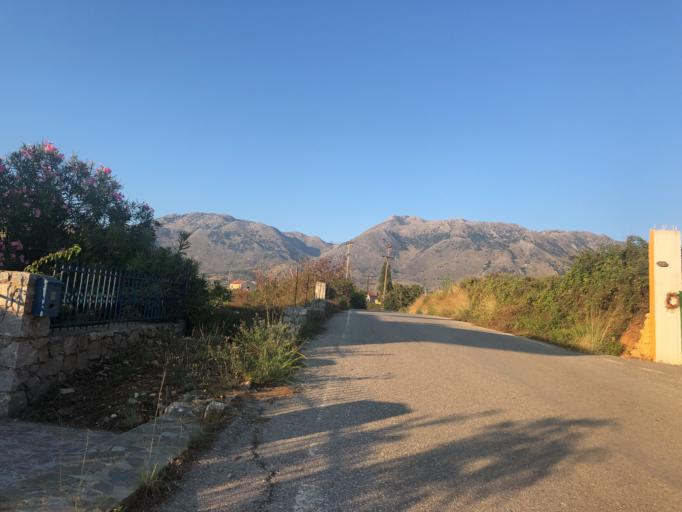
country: GR
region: Crete
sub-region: Nomos Chanias
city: Georgioupolis
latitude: 35.3447
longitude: 24.3021
